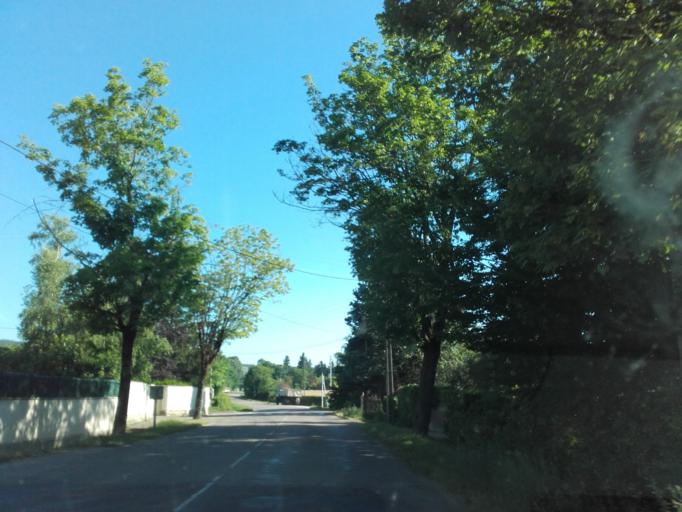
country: FR
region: Bourgogne
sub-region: Departement de Saone-et-Loire
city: Givry
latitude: 46.7695
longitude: 4.7384
